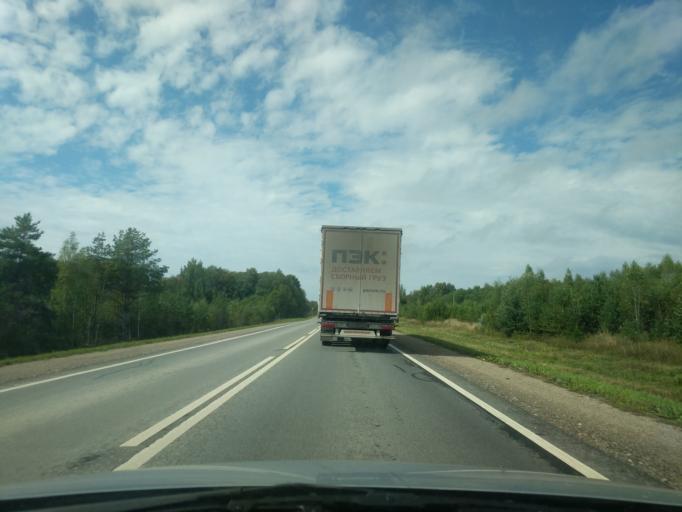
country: RU
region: Kostroma
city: Sudislavl'
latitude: 57.8623
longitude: 41.7686
